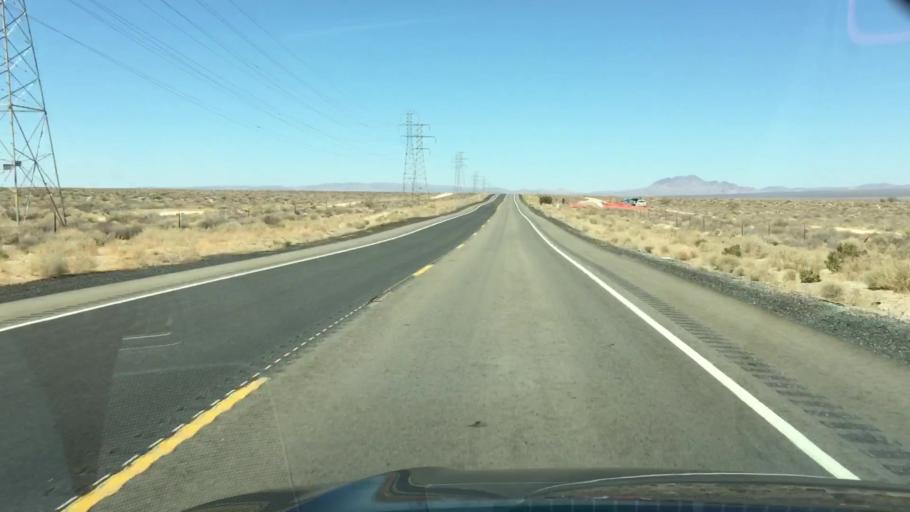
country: US
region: California
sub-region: Kern County
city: Boron
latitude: 35.1019
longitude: -117.5721
